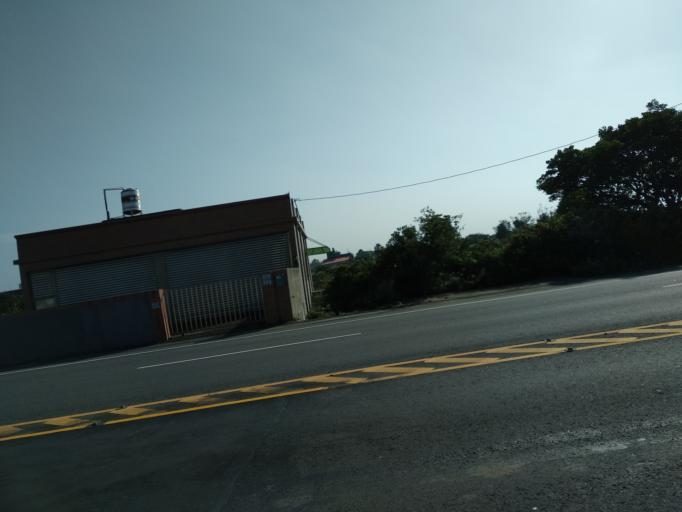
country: TW
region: Taiwan
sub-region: Hsinchu
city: Zhubei
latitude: 24.9835
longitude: 121.0580
